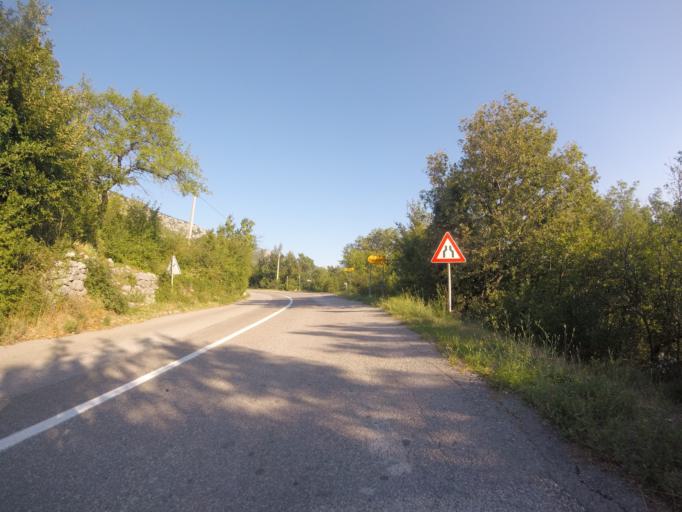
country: HR
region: Primorsko-Goranska
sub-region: Grad Crikvenica
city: Crikvenica
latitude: 45.2153
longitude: 14.7005
